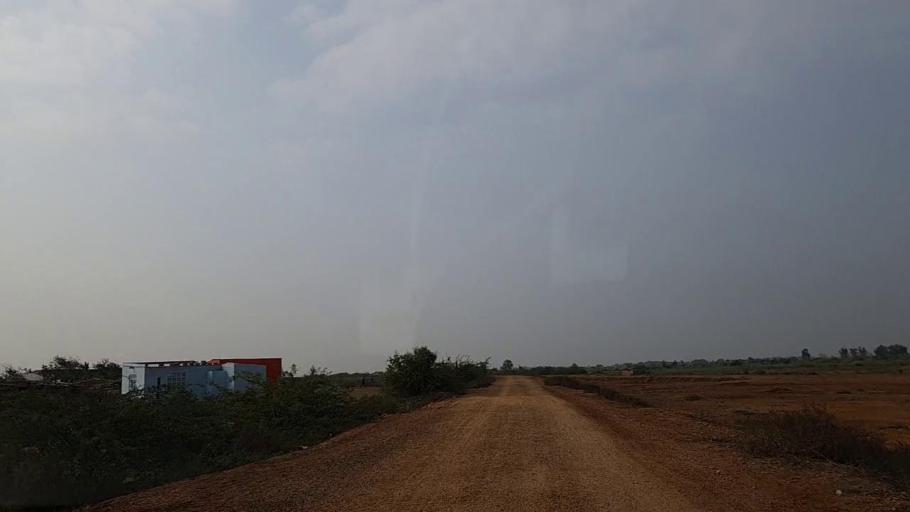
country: PK
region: Sindh
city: Thatta
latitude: 24.7408
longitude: 67.8409
